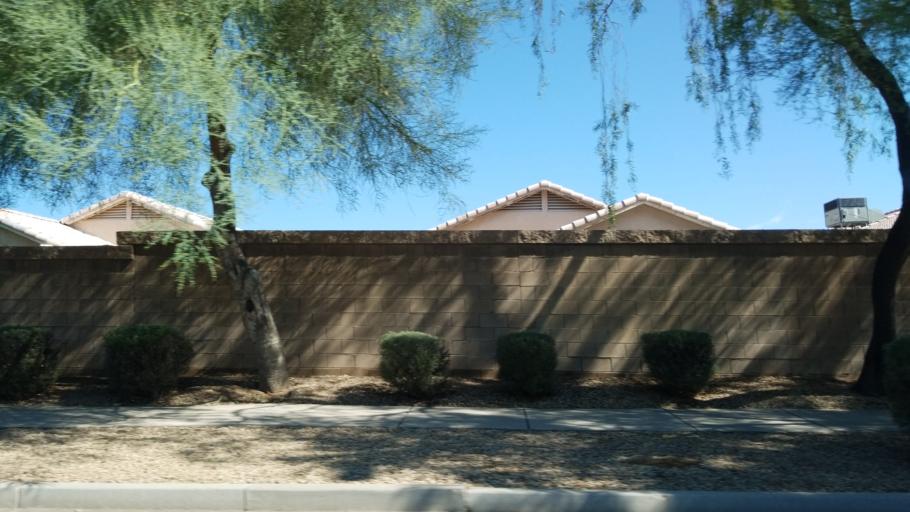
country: US
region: Arizona
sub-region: Maricopa County
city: Peoria
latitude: 33.6839
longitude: -112.1373
